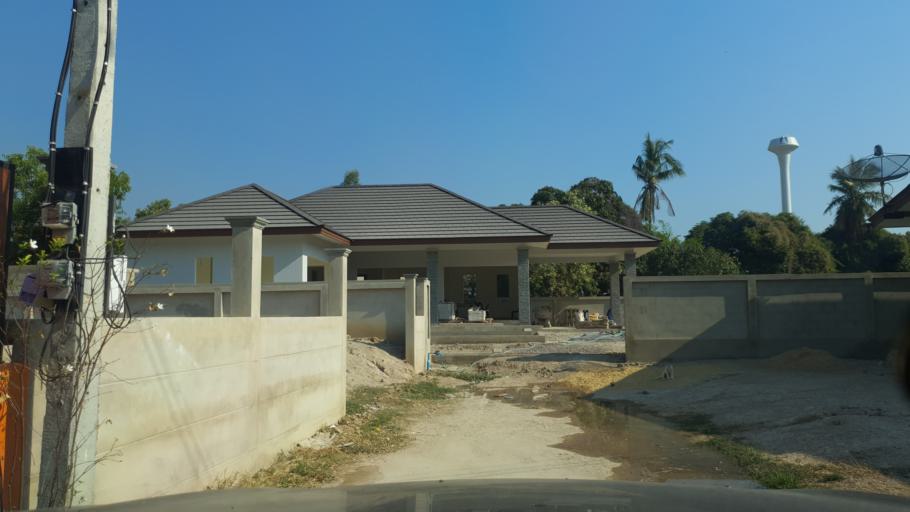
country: TH
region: Phetchaburi
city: Cha-am
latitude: 12.7821
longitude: 99.9765
